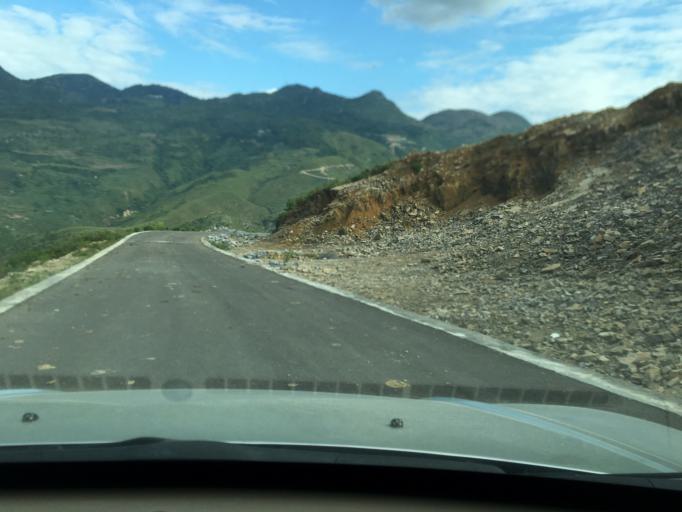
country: CN
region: Guizhou Sheng
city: Anshun
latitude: 25.7774
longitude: 105.3800
